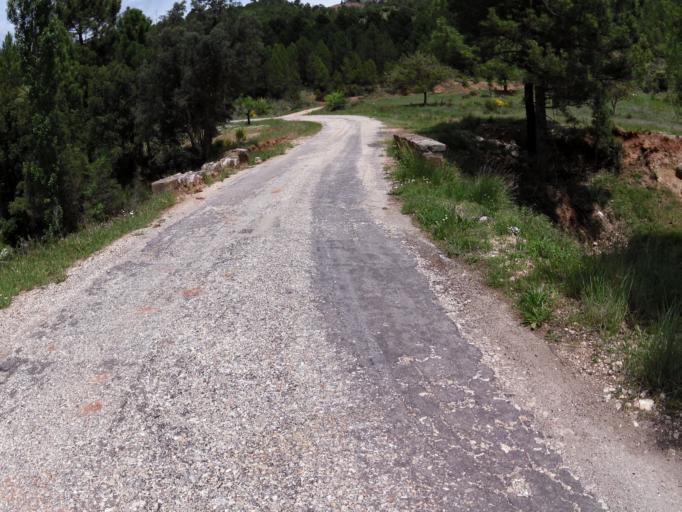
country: ES
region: Castille-La Mancha
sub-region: Provincia de Albacete
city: Paterna del Madera
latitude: 38.5787
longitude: -2.3422
